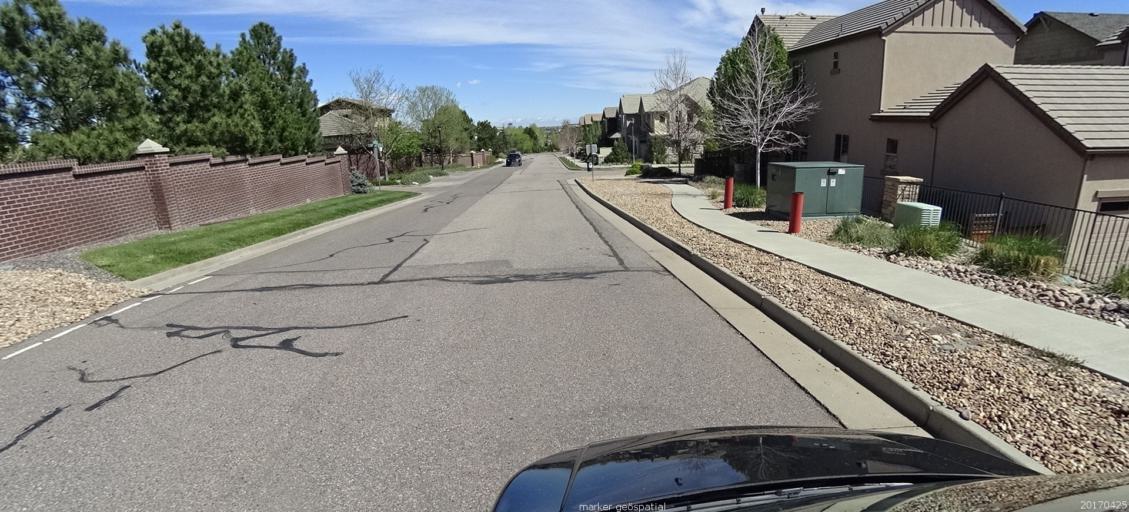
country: US
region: Colorado
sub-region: Douglas County
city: Carriage Club
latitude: 39.5314
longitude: -104.8857
